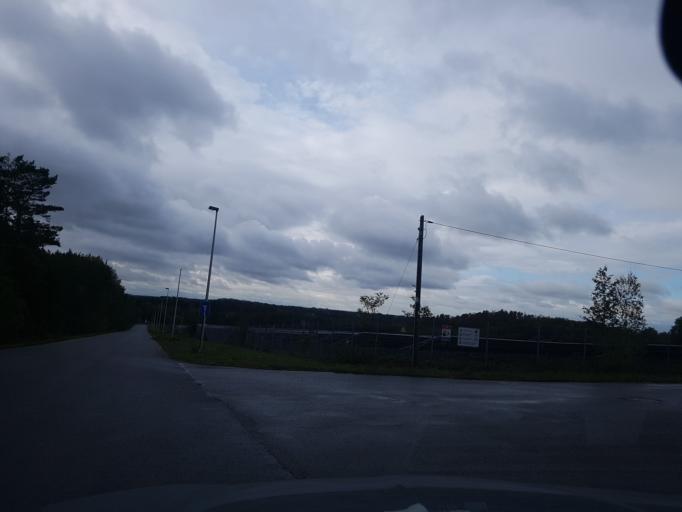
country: DE
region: Brandenburg
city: Elsterwerda
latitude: 51.4817
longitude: 13.4842
